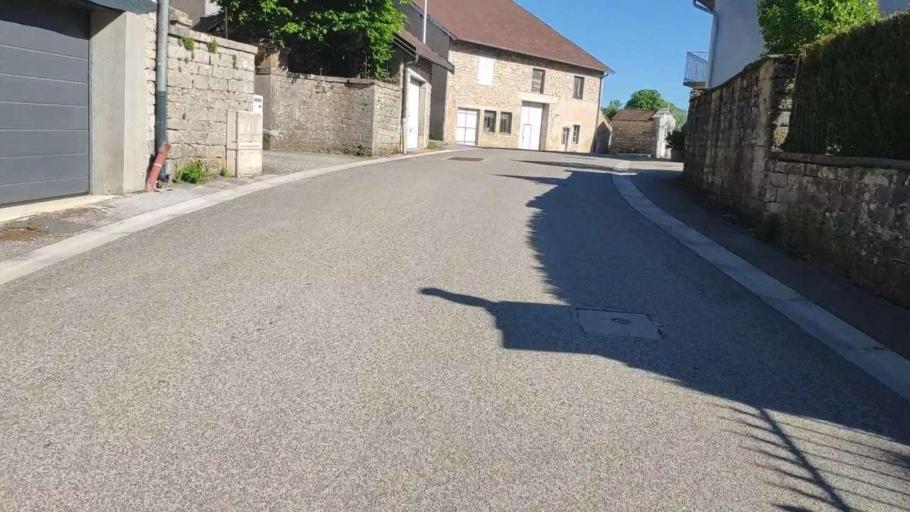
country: FR
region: Franche-Comte
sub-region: Departement du Jura
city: Perrigny
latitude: 46.6870
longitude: 5.6585
